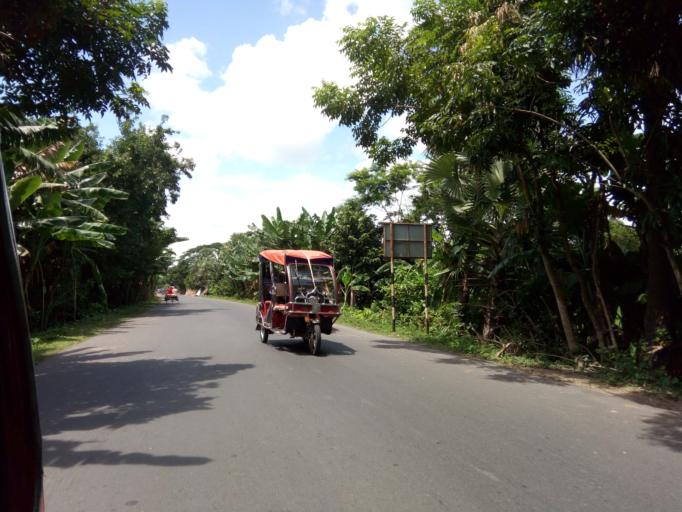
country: BD
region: Dhaka
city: Tungipara
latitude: 22.9059
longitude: 89.8803
